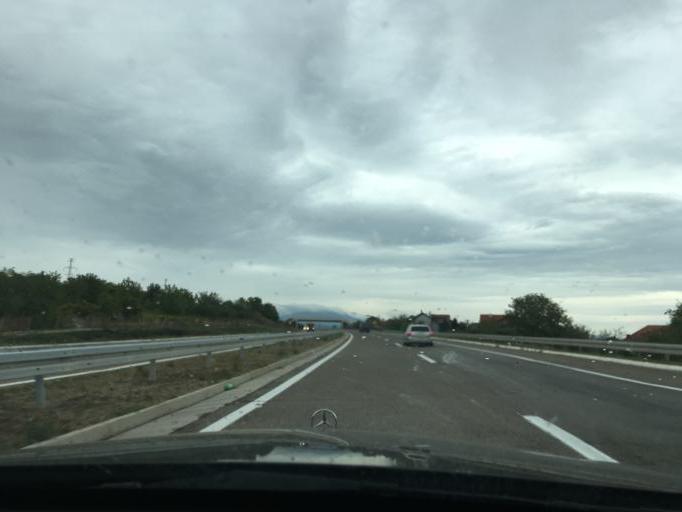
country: RS
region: Central Serbia
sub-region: Nisavski Okrug
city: Nis
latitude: 43.3413
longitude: 21.9091
